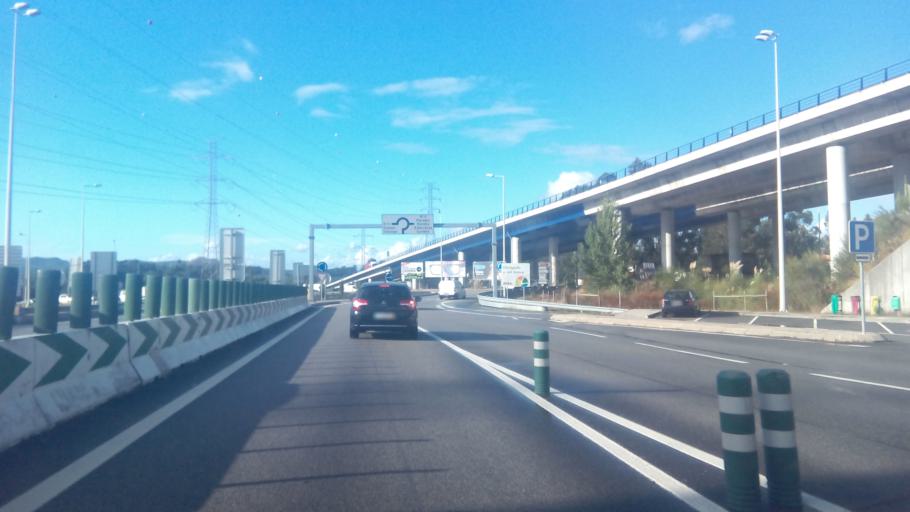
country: PT
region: Porto
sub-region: Valongo
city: Campo
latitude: 41.1840
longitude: -8.4547
